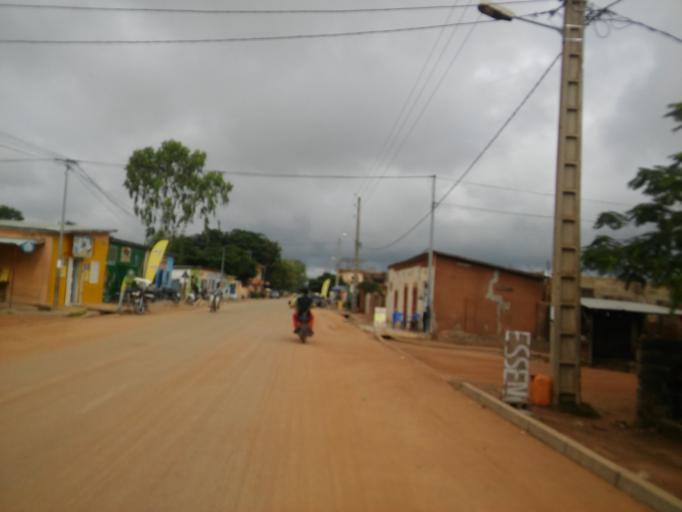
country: BJ
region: Borgou
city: Parakou
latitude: 9.3514
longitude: 2.6293
